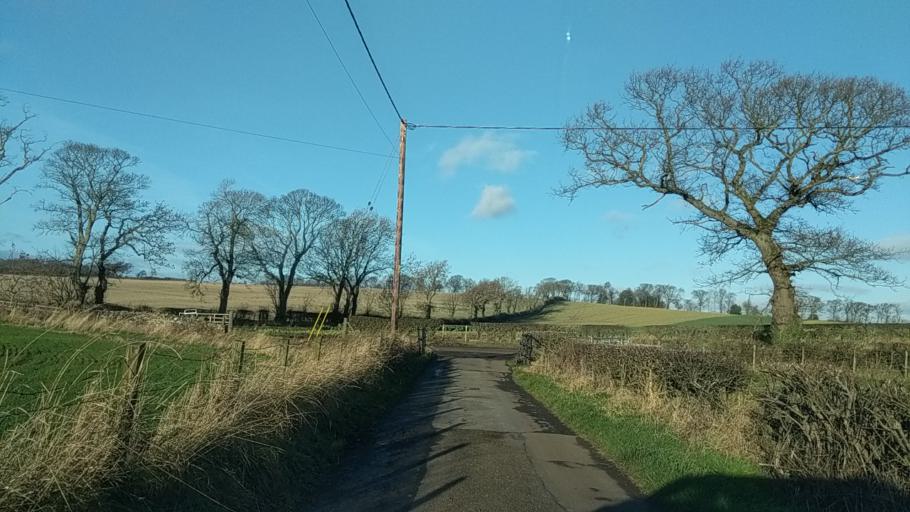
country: GB
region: Scotland
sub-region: West Lothian
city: Linlithgow
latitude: 55.9974
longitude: -3.5453
